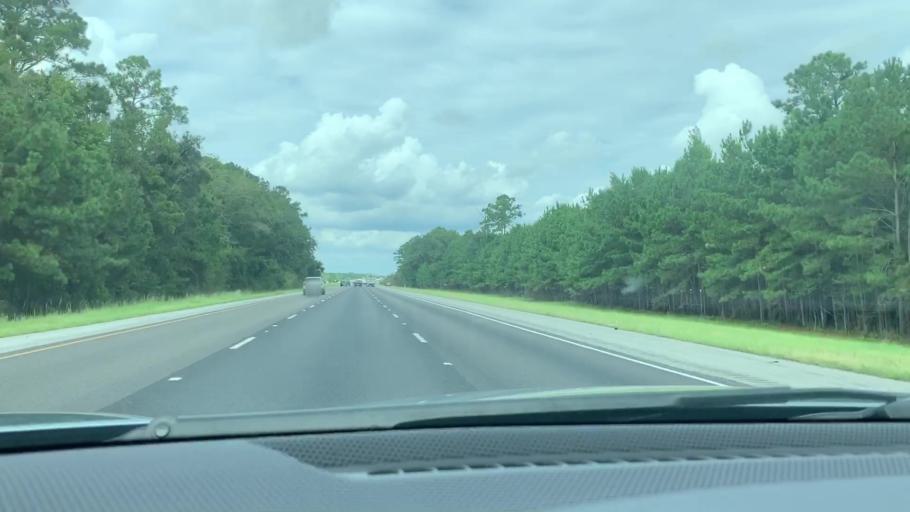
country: US
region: Georgia
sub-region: Liberty County
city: Midway
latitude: 31.7239
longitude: -81.3886
